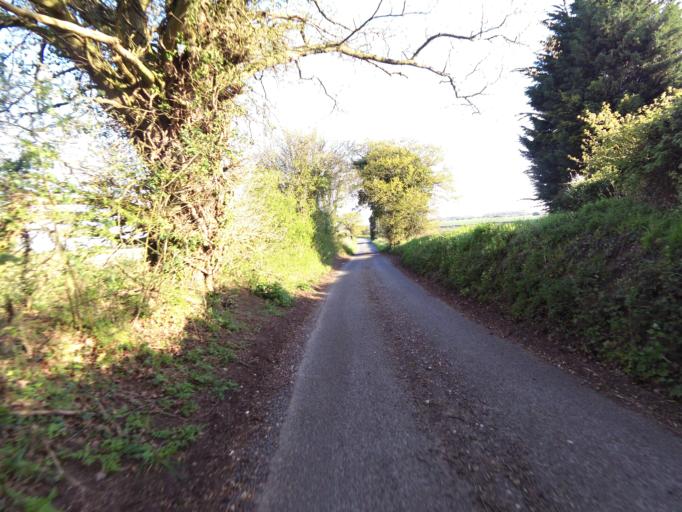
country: GB
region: England
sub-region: Suffolk
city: Bramford
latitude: 52.0468
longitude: 1.0637
